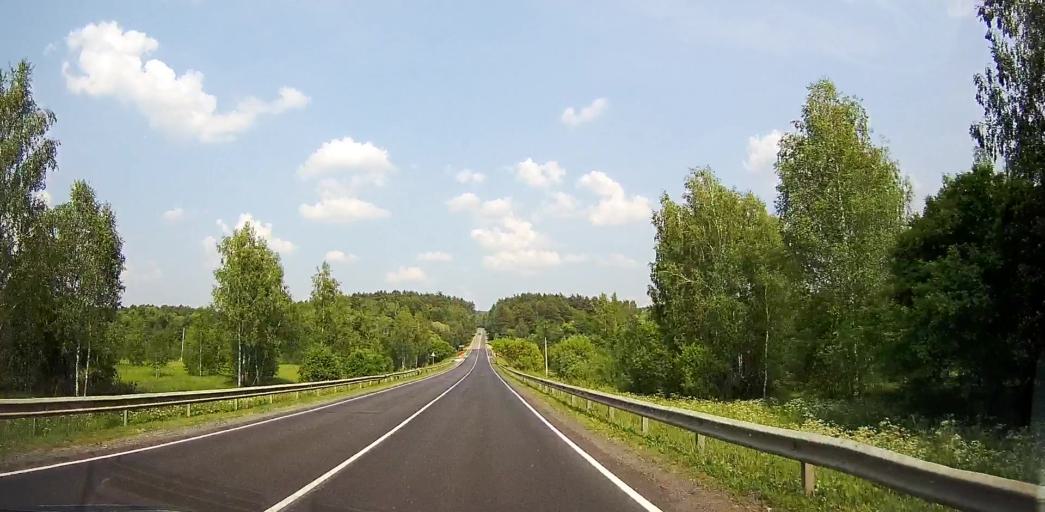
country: RU
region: Moskovskaya
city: Stupino
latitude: 54.9683
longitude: 38.1369
